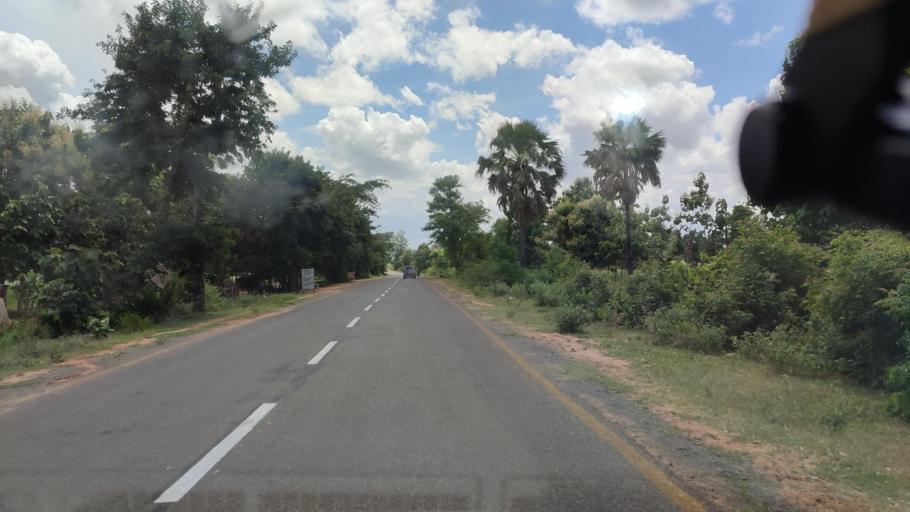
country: MM
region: Magway
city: Magway
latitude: 20.1904
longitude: 95.0529
